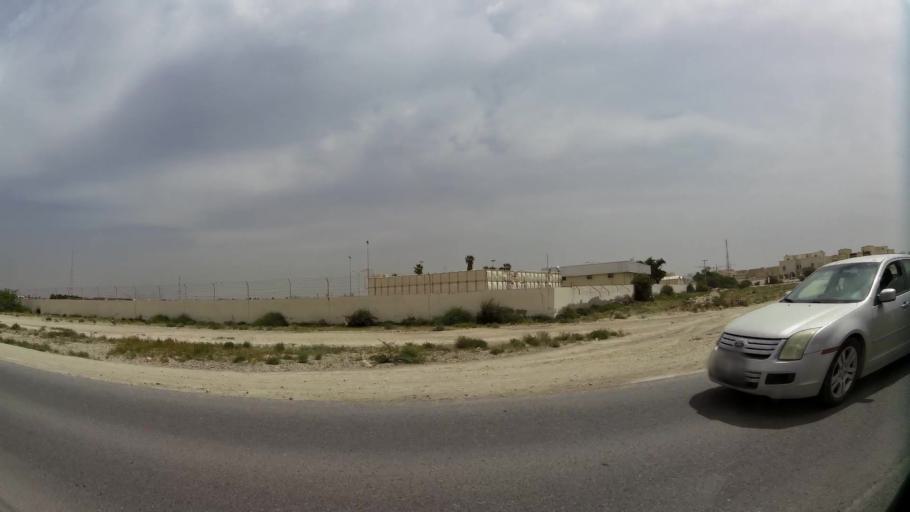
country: QA
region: Baladiyat ar Rayyan
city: Ar Rayyan
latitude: 25.2715
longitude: 51.4611
